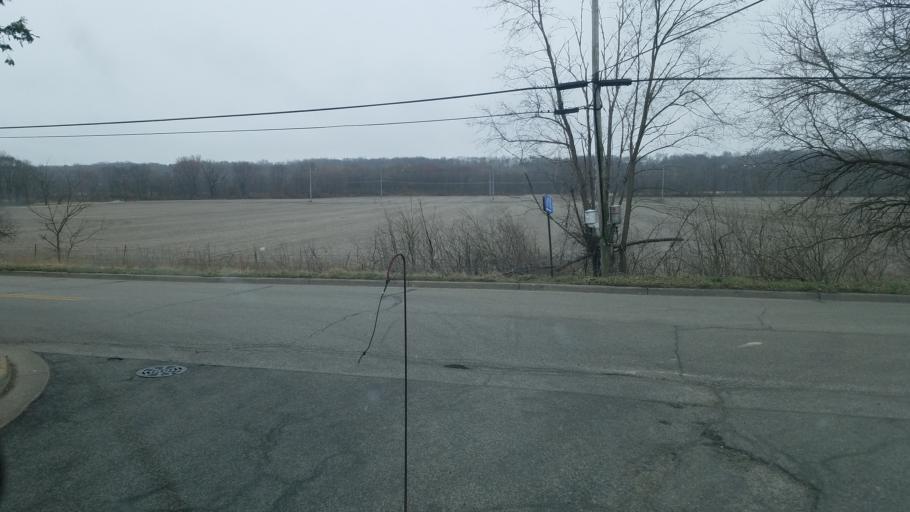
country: US
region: Indiana
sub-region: Wabash County
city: Wabash
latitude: 40.7984
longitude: -85.8424
